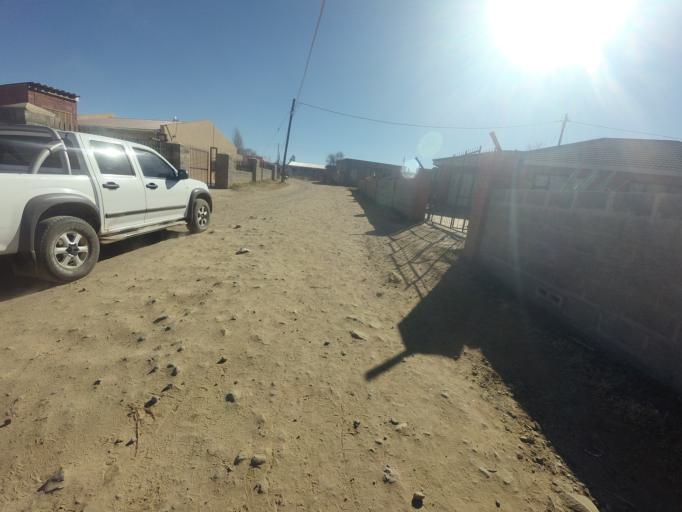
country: LS
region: Maseru
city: Maseru
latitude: -29.2976
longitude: 27.5412
